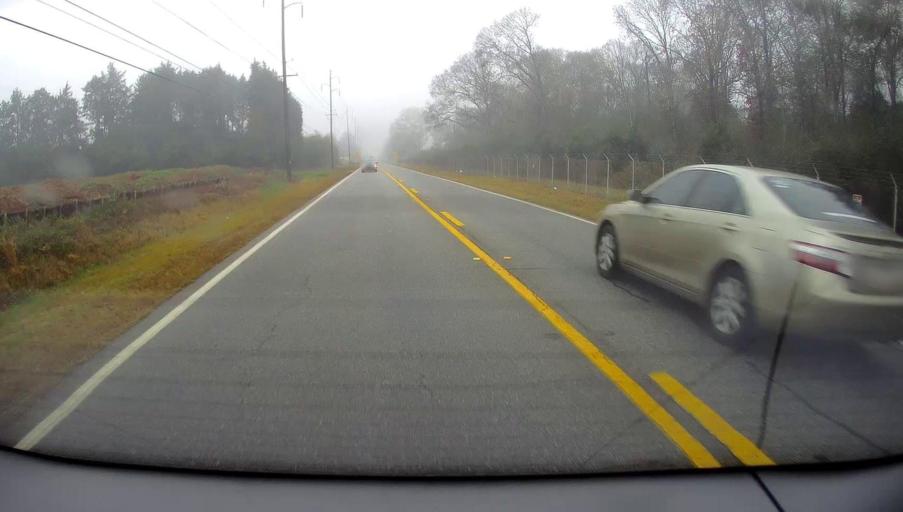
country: US
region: Georgia
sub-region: Houston County
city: Centerville
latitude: 32.6538
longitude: -83.7088
